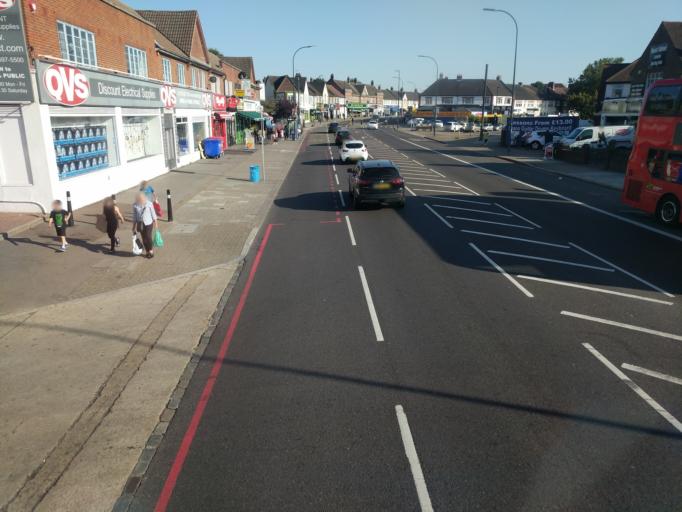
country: GB
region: England
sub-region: Greater London
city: Catford
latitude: 51.4262
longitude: -0.0064
